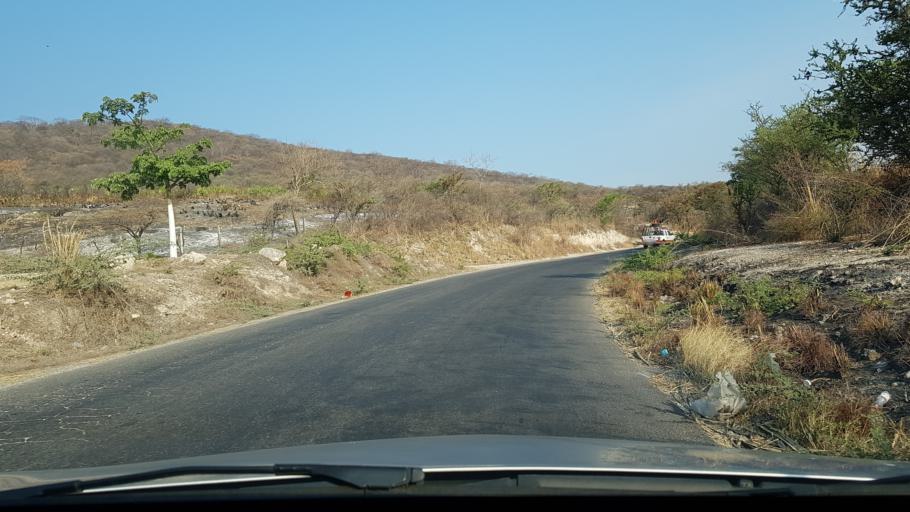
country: MX
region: Morelos
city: Tlaltizapan
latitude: 18.6581
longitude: -99.0449
